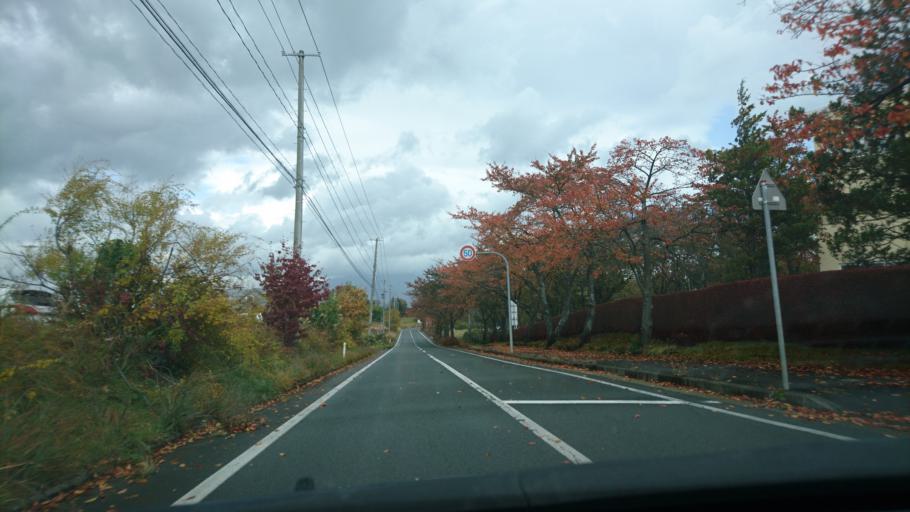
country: JP
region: Iwate
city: Shizukuishi
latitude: 39.6898
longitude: 141.0234
